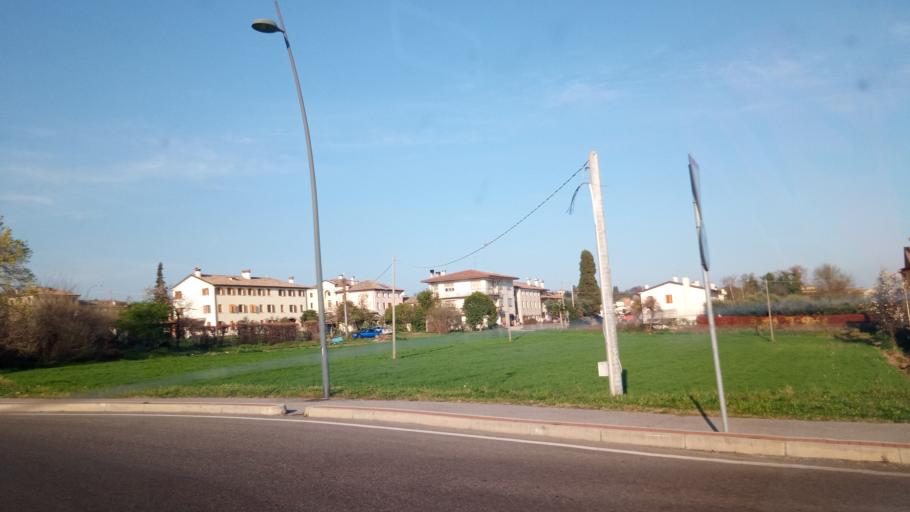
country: IT
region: Veneto
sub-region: Provincia di Treviso
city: Crespano del Grappa
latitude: 45.8218
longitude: 11.8297
